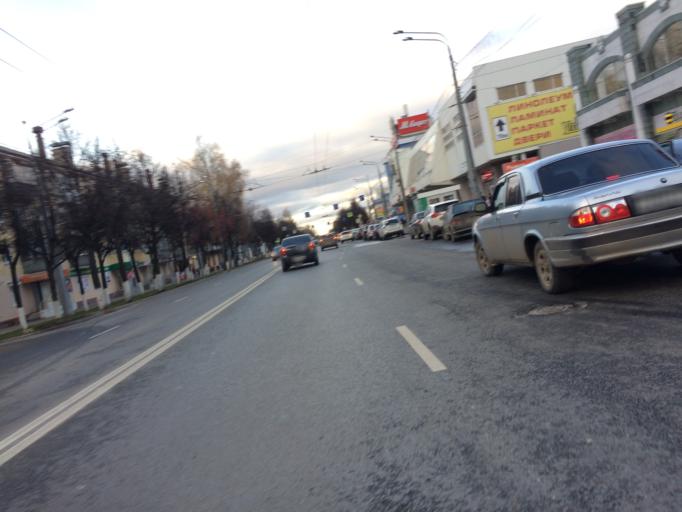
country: RU
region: Mariy-El
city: Yoshkar-Ola
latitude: 56.6334
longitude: 47.8840
